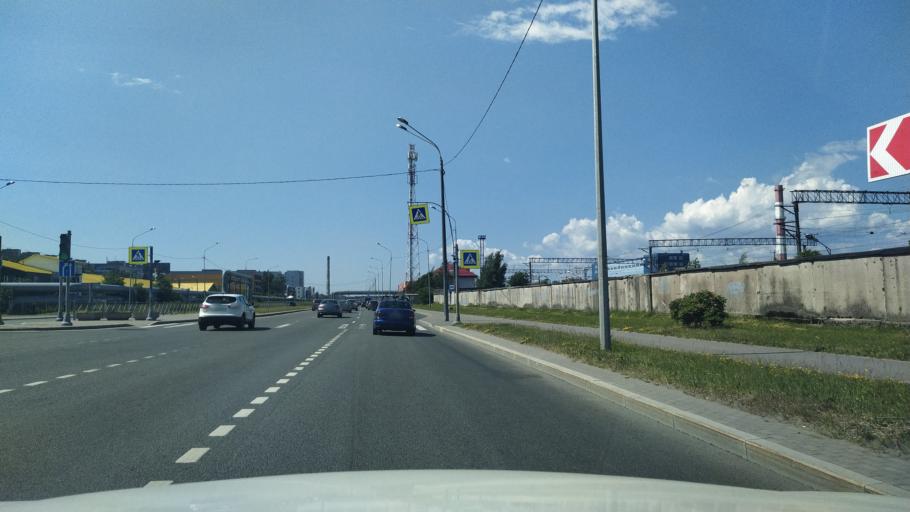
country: RU
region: Leningrad
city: Parnas
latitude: 60.0567
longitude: 30.3607
